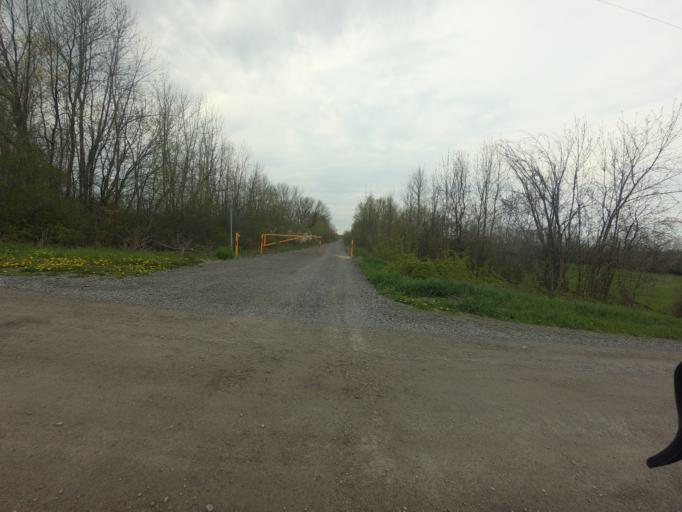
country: CA
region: Ontario
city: Carleton Place
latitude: 45.2117
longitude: -76.1778
